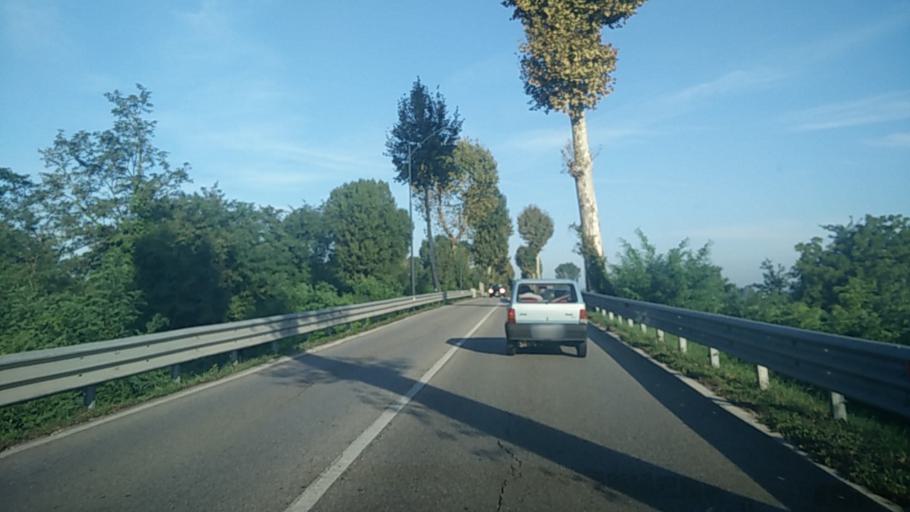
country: IT
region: Veneto
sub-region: Provincia di Venezia
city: Zelarino
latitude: 45.5194
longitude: 12.2001
